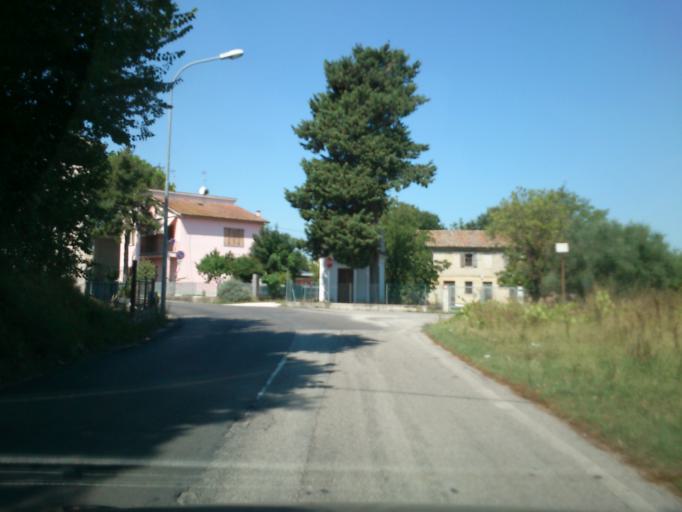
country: IT
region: The Marches
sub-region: Provincia di Pesaro e Urbino
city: Lucrezia
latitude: 43.7725
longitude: 12.9435
